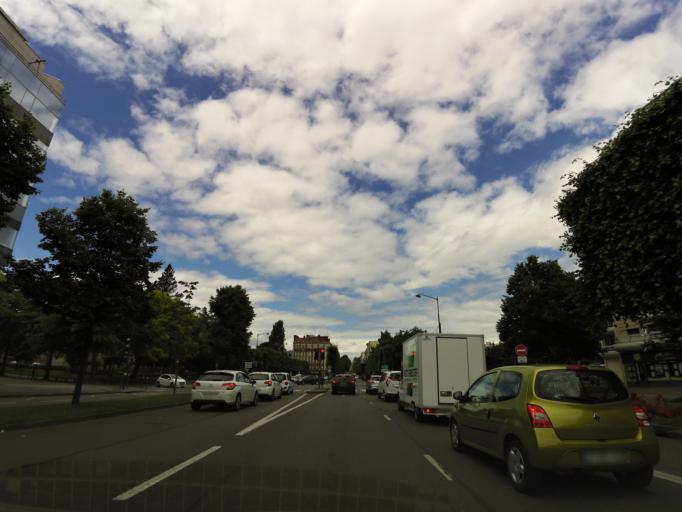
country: FR
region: Brittany
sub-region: Departement d'Ille-et-Vilaine
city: Rennes
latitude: 48.1050
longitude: -1.6845
